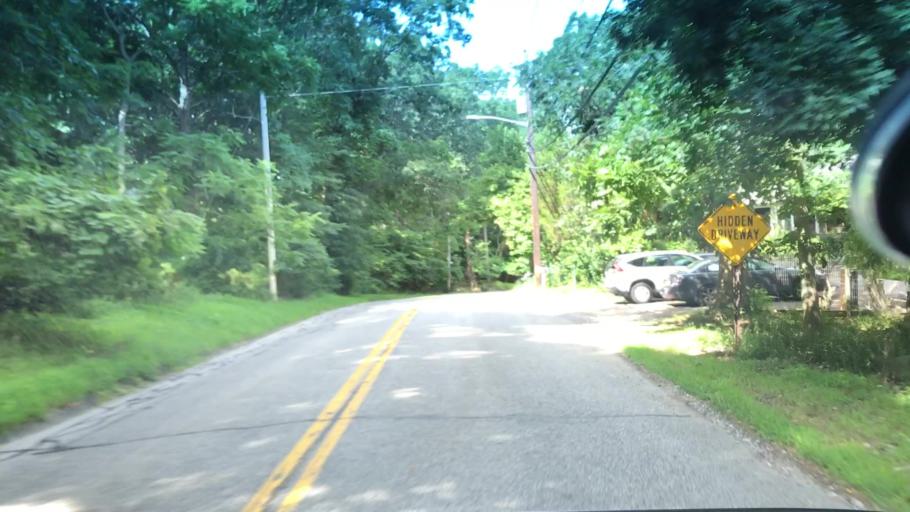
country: US
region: New York
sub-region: Suffolk County
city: Wading River
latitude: 40.9593
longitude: -72.8360
